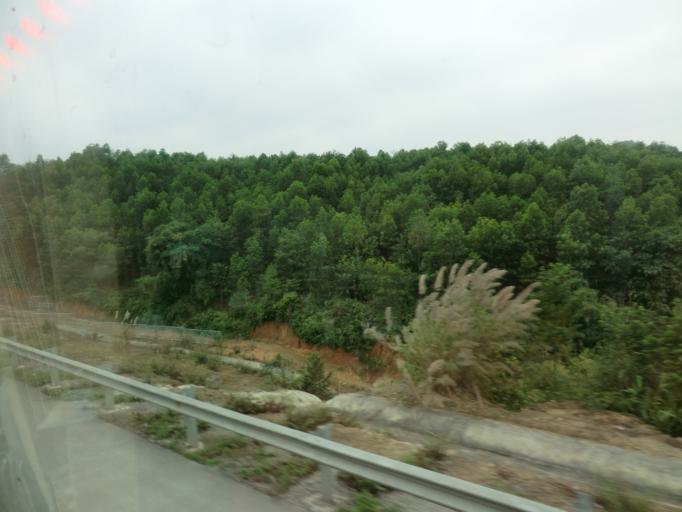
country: VN
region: Yen Bai
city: Yen Bai
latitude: 21.6588
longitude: 104.8851
